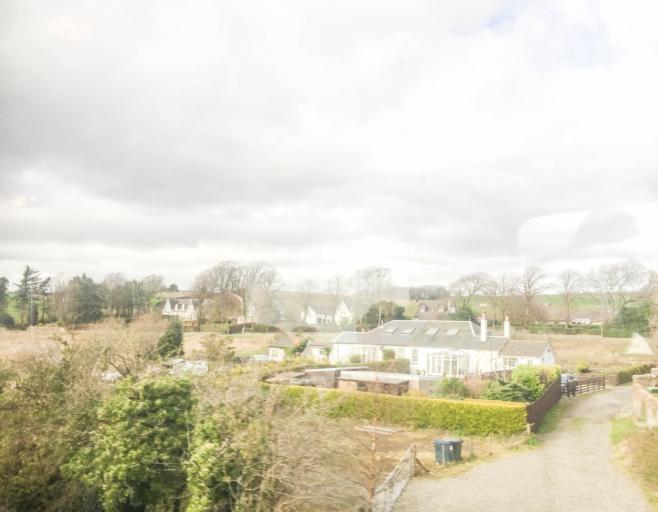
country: GB
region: Scotland
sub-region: Argyll and Bute
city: Cardross
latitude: 55.9515
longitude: -4.6231
